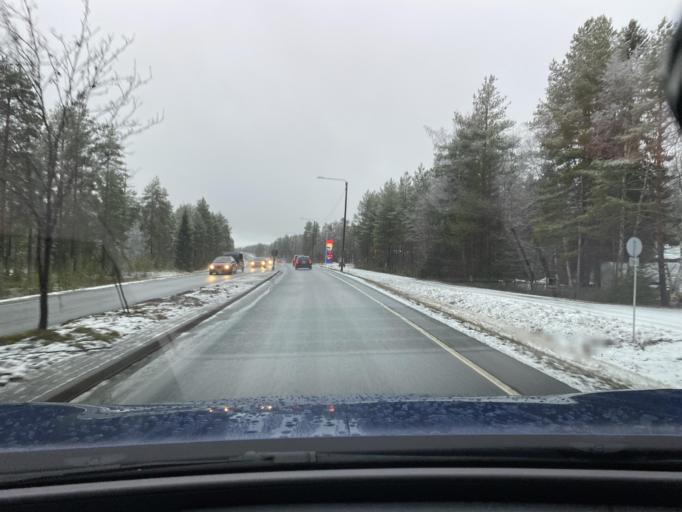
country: FI
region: Northern Ostrobothnia
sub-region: Oulu
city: Kiiminki
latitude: 65.1274
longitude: 25.7717
